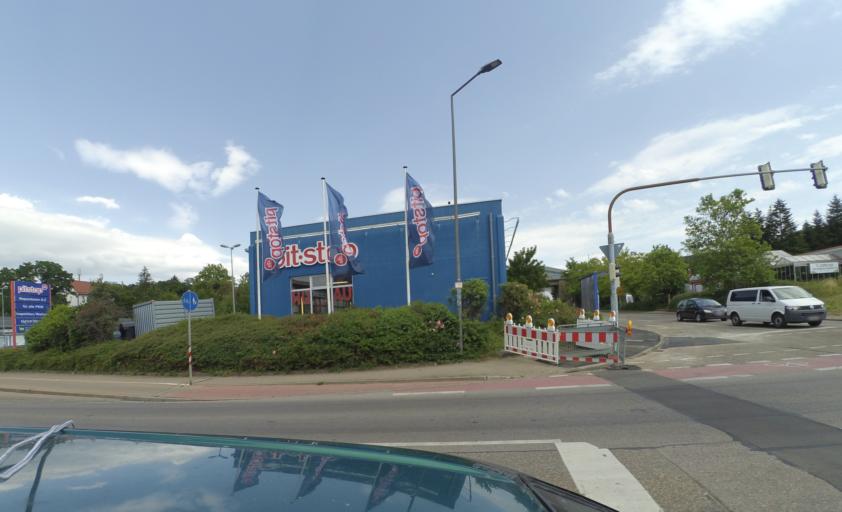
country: DE
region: Baden-Wuerttemberg
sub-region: Regierungsbezirk Stuttgart
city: Aalen
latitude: 48.8573
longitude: 10.1015
